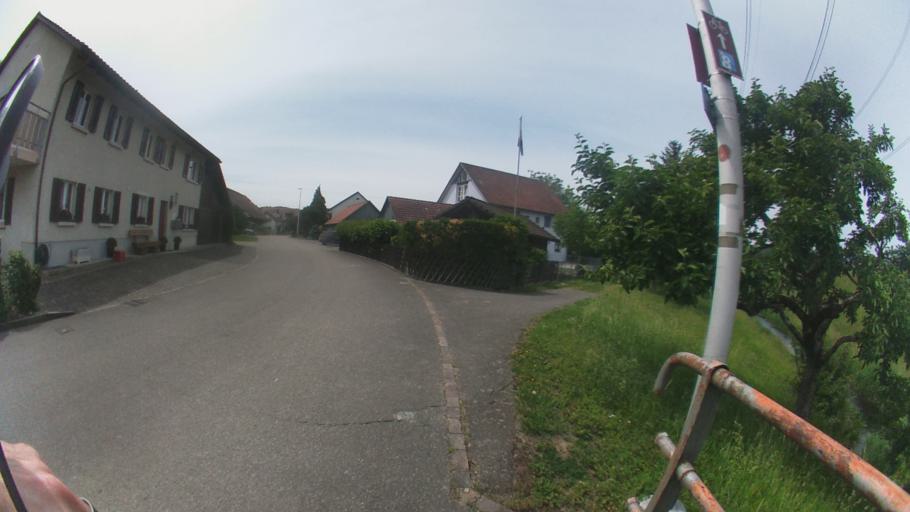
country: CH
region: Aargau
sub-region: Bezirk Zurzach
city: Koblenz
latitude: 47.5885
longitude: 8.2267
